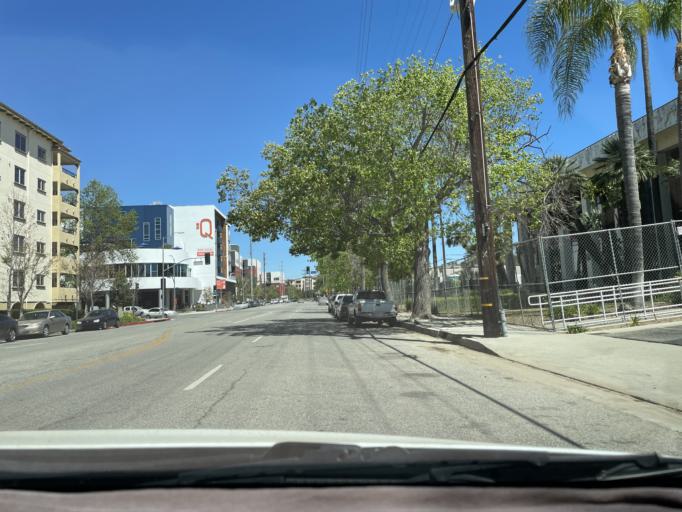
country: US
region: California
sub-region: Los Angeles County
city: Canoga Park
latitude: 34.1828
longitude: -118.5937
